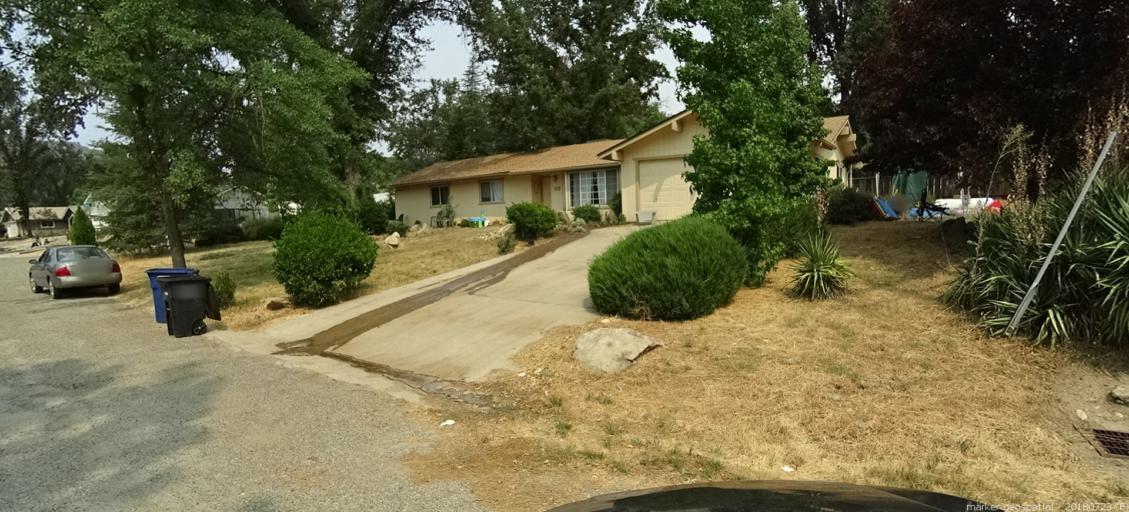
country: US
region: California
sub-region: Madera County
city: Ahwahnee
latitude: 37.3364
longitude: -119.7065
